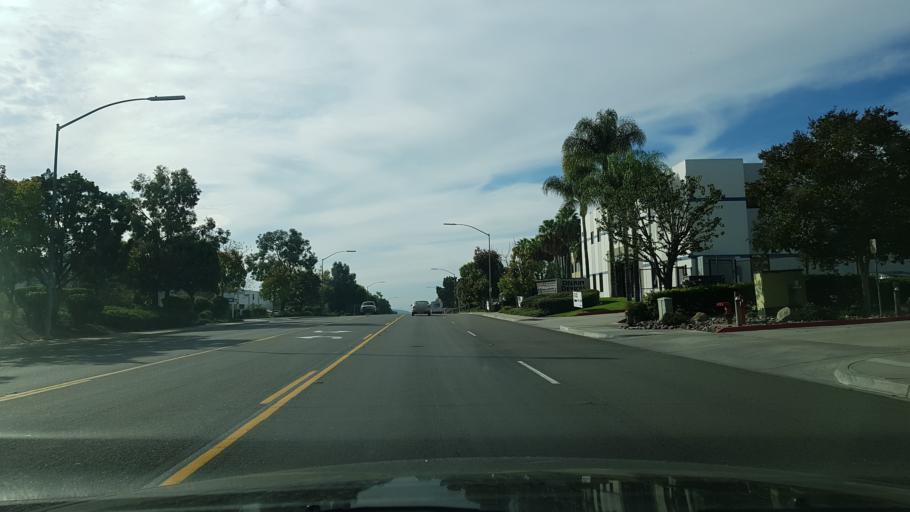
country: US
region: California
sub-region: San Diego County
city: Poway
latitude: 32.9349
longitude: -117.0412
